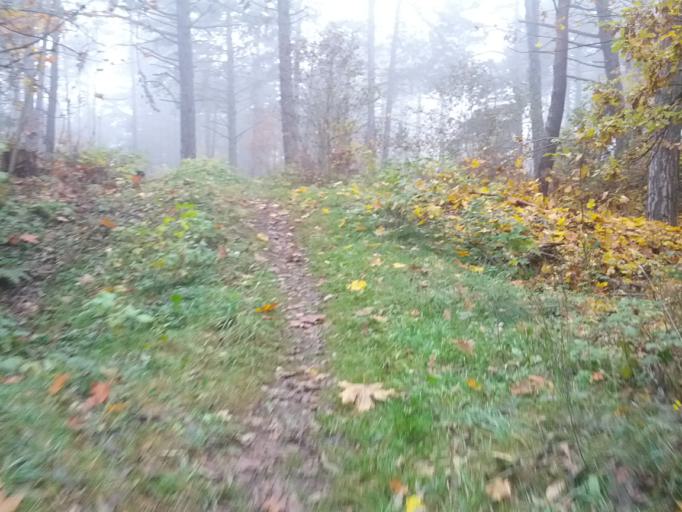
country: DE
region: Thuringia
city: Eisenach
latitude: 50.9724
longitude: 10.3568
